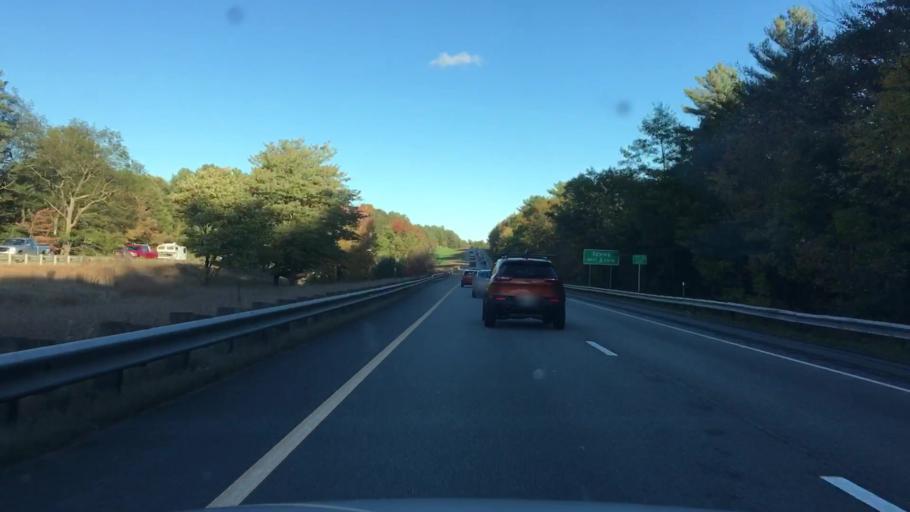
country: US
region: New Hampshire
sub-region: Rockingham County
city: Raymond
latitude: 43.0311
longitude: -71.1460
